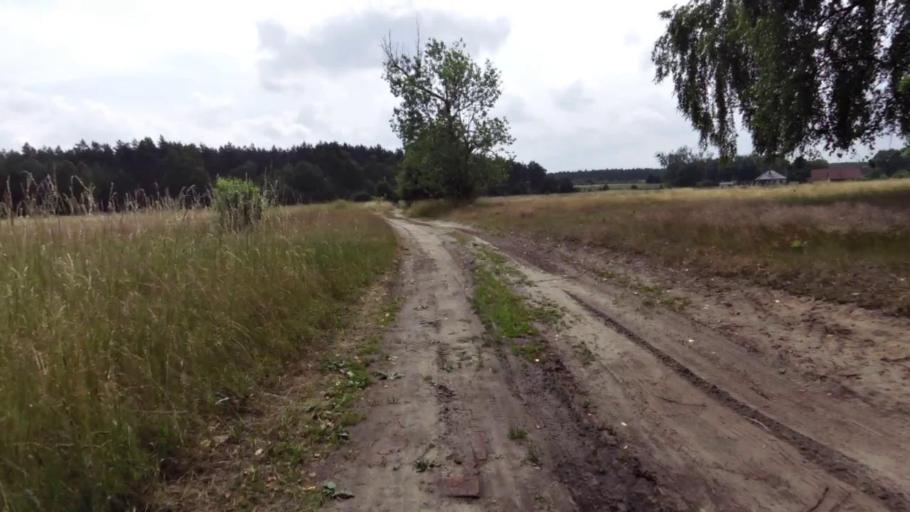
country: PL
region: West Pomeranian Voivodeship
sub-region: Powiat kamienski
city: Wolin
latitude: 53.7564
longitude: 14.6594
